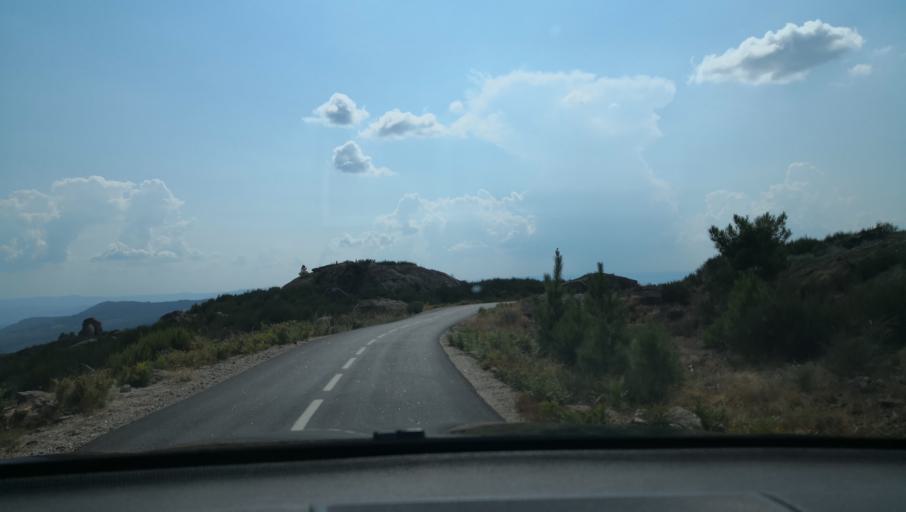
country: PT
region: Vila Real
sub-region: Sabrosa
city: Sabrosa
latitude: 41.2881
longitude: -7.6132
